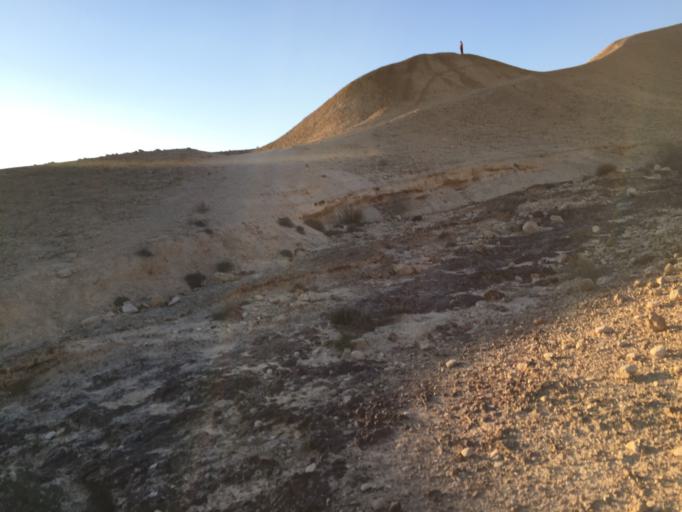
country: IL
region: Southern District
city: Midreshet Ben-Gurion
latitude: 30.8449
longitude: 34.7564
